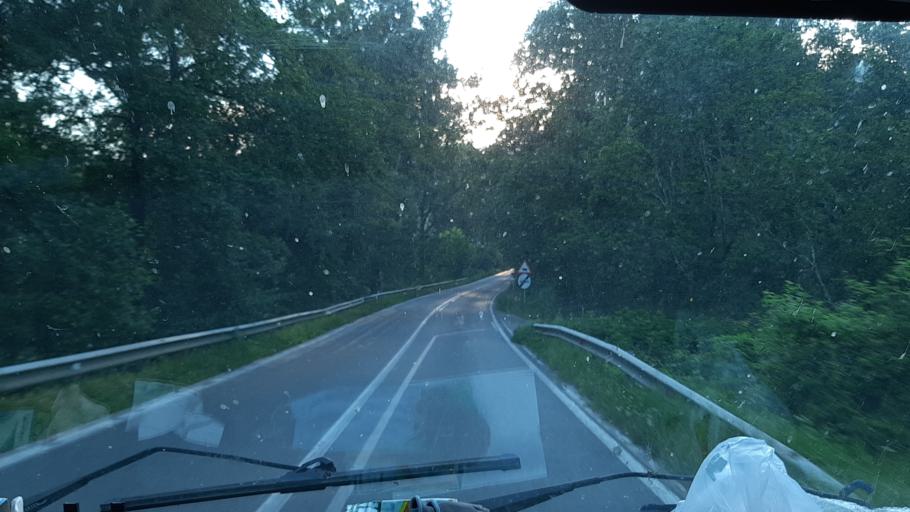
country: RO
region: Caras-Severin
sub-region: Municipiul Resita
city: Calnic
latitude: 45.3671
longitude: 21.8080
